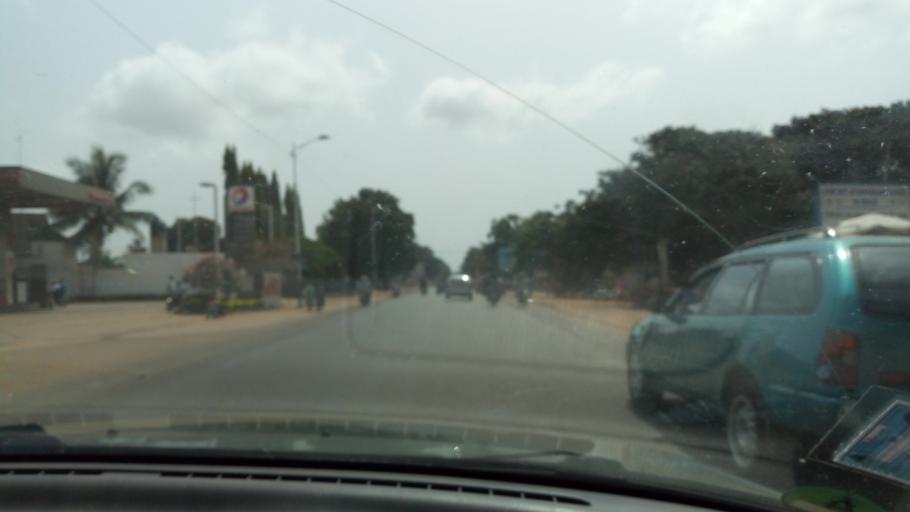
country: TG
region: Maritime
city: Lome
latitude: 6.1732
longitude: 1.1863
